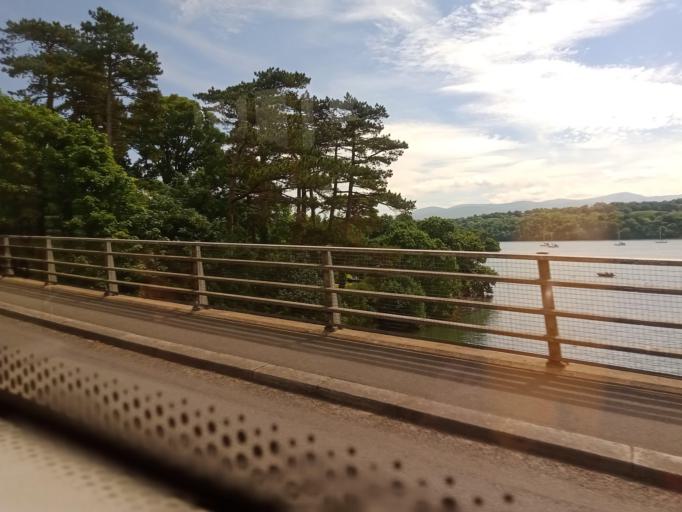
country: GB
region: Wales
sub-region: Anglesey
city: Menai Bridge
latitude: 53.2328
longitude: -4.1582
